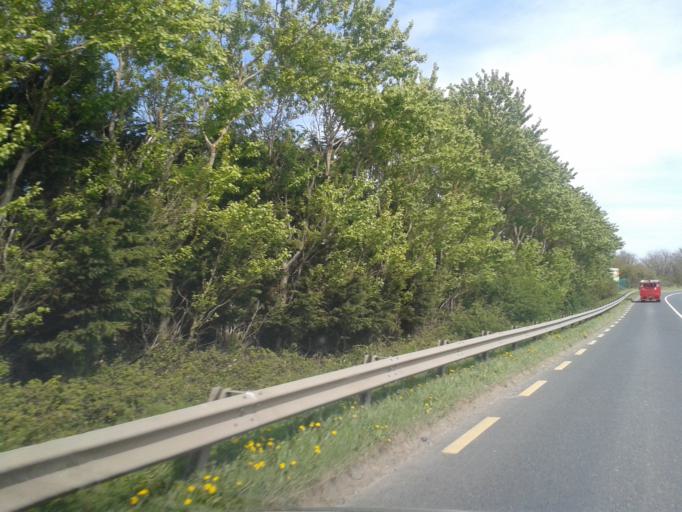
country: IE
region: Leinster
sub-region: Fingal County
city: Swords
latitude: 53.4374
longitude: -6.2423
